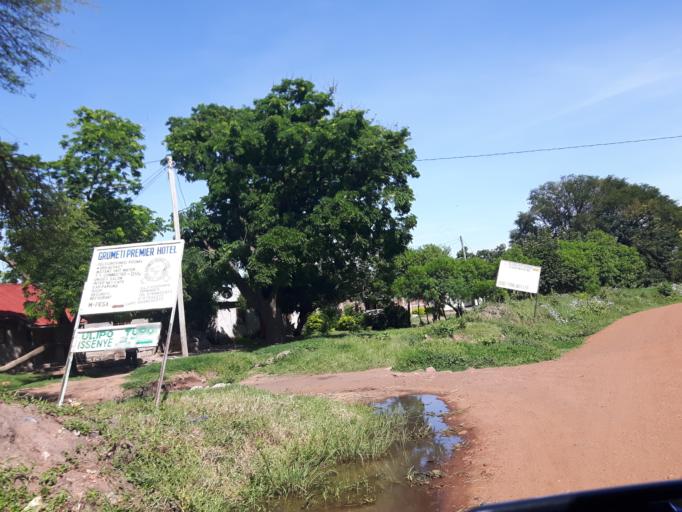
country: TZ
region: Mara
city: Issenye
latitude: -1.9891
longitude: 34.3476
